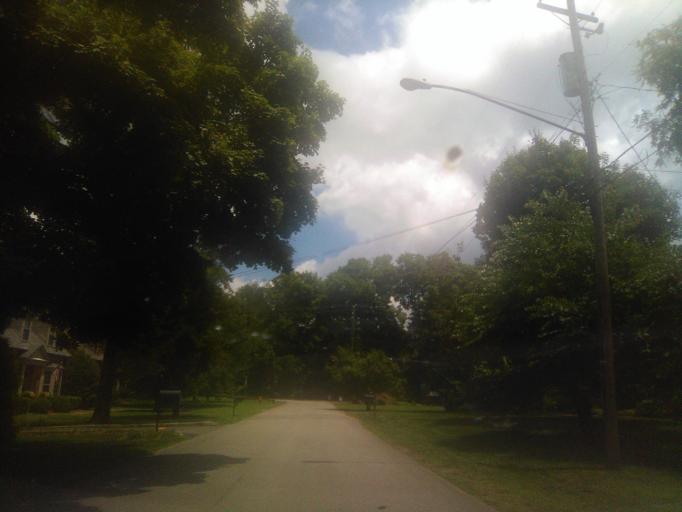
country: US
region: Tennessee
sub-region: Davidson County
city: Belle Meade
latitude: 36.1141
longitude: -86.8285
